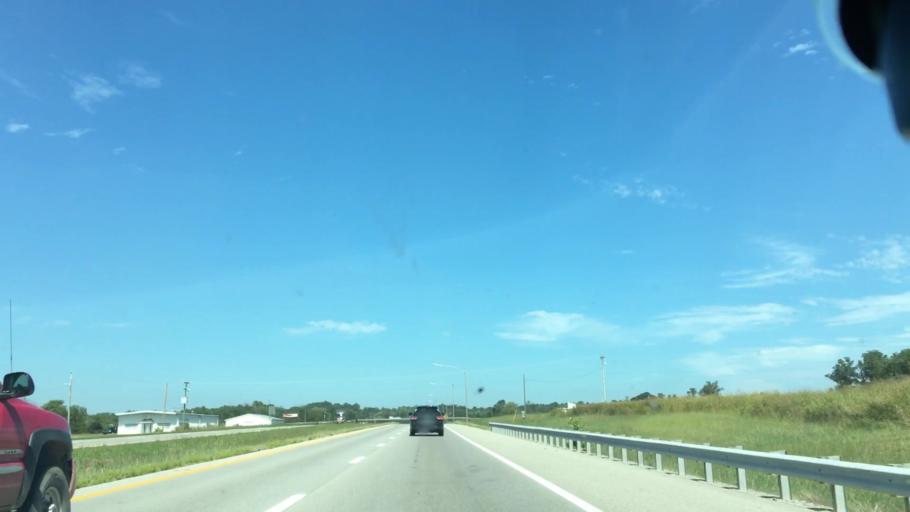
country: US
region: Kentucky
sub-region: Christian County
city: Hopkinsville
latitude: 36.8893
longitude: -87.4688
